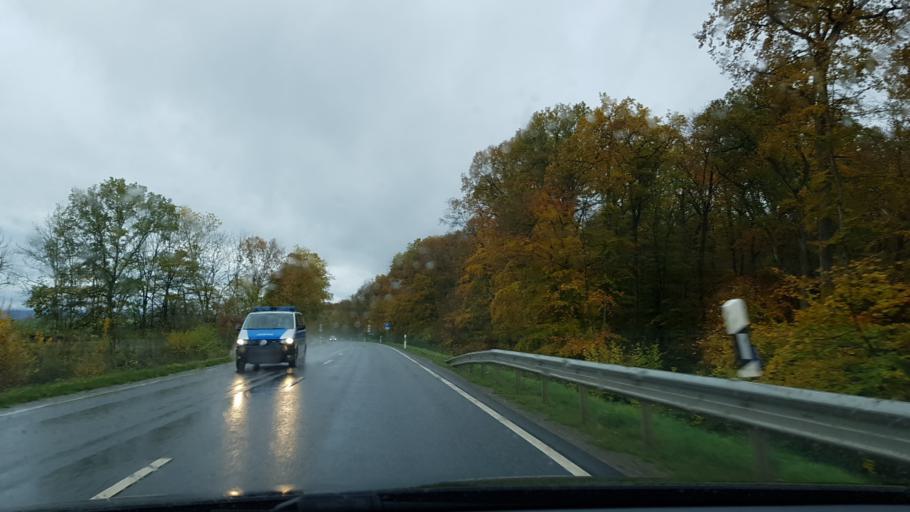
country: DE
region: Rheinland-Pfalz
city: Sehlem
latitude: 49.9132
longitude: 6.8284
